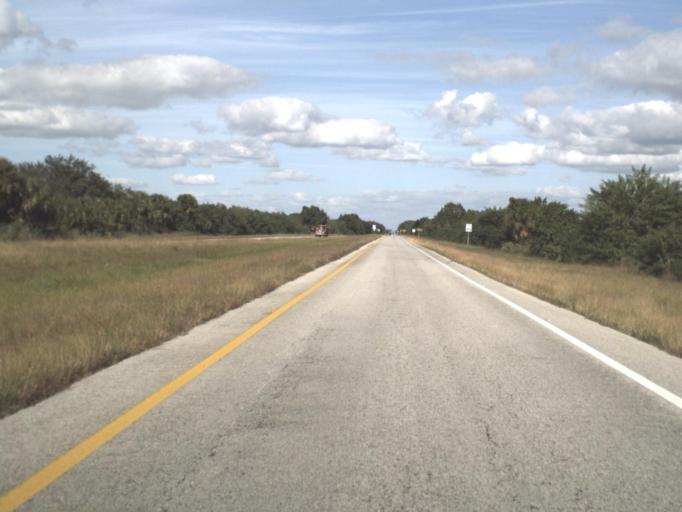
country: US
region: Florida
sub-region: Brevard County
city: Port Saint John
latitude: 28.4552
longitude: -80.8703
